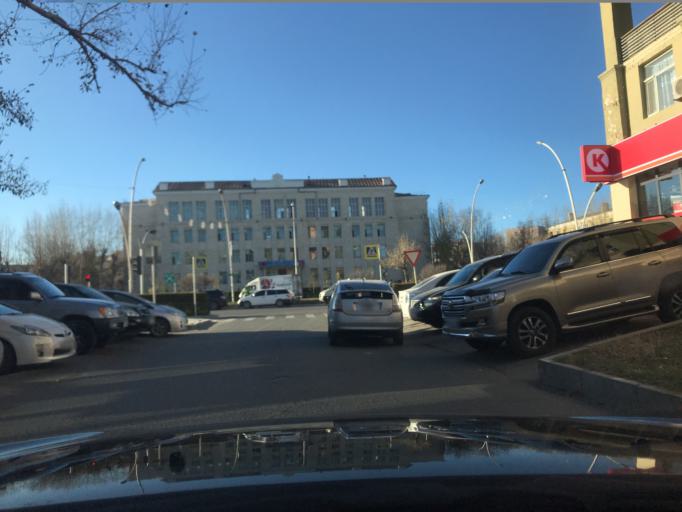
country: MN
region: Ulaanbaatar
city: Ulaanbaatar
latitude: 47.9244
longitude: 106.9127
